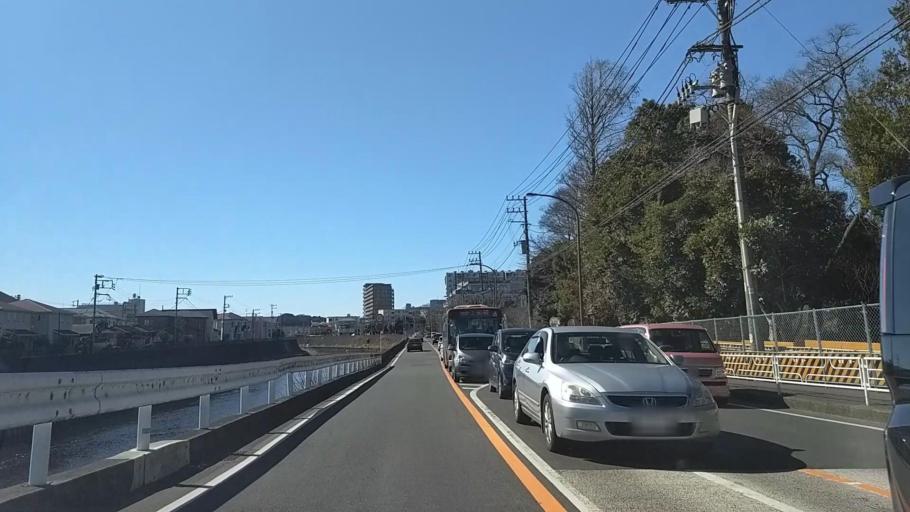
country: JP
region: Kanagawa
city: Kamakura
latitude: 35.3473
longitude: 139.5221
